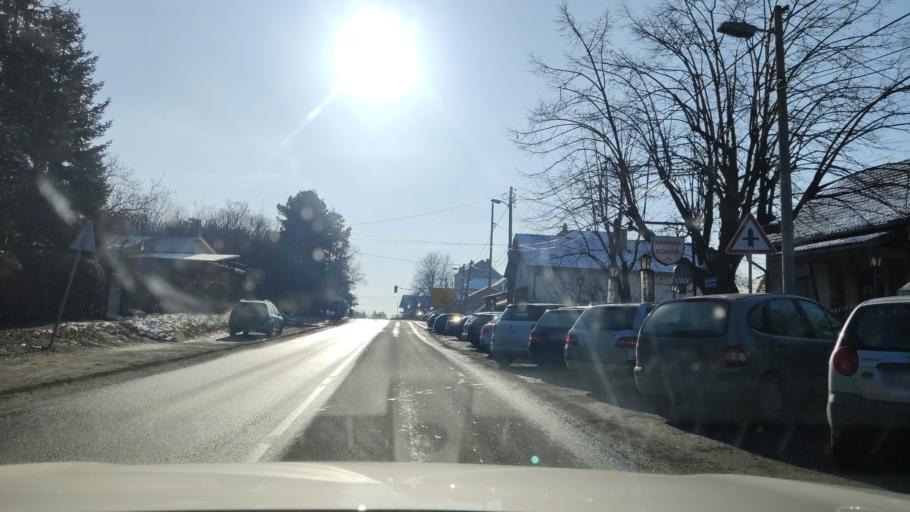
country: RS
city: Rusanj
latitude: 44.6975
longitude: 20.5022
